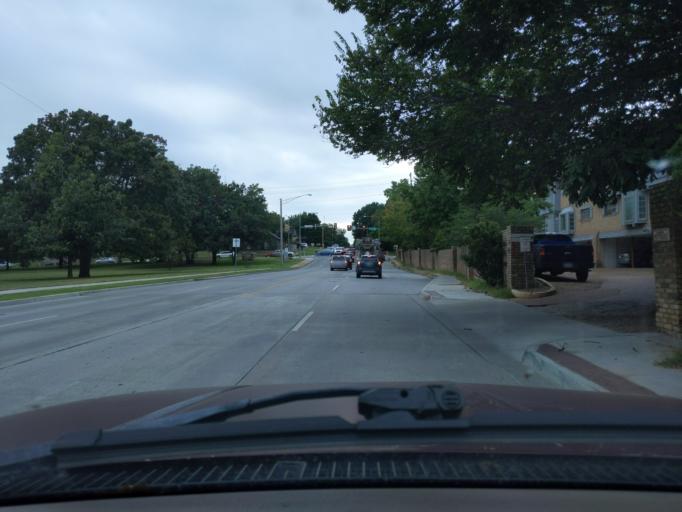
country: US
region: Oklahoma
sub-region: Tulsa County
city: Tulsa
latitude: 36.1334
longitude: -95.9743
